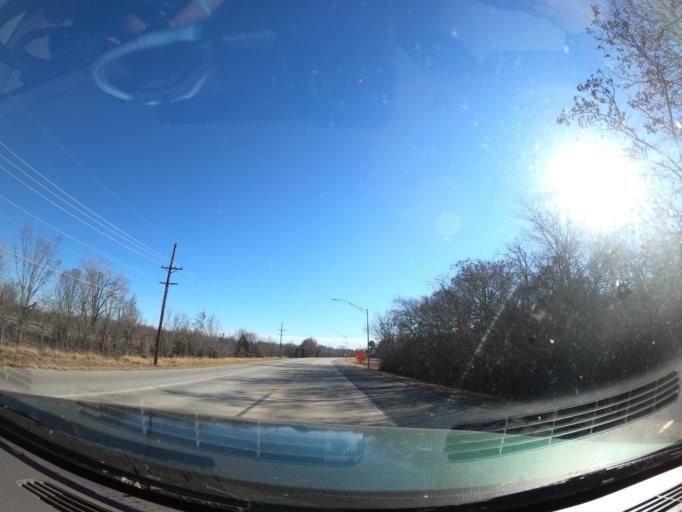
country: US
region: Oklahoma
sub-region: McIntosh County
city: Eufaula
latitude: 35.2987
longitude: -95.5834
